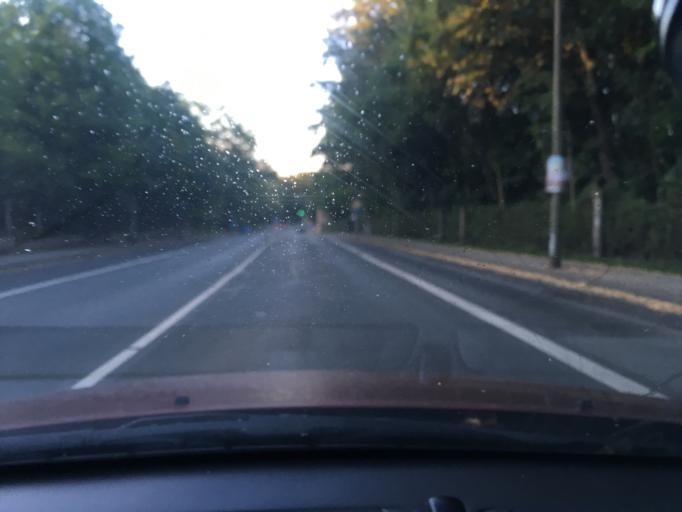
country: DE
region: Saxony
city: Goerlitz
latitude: 51.1497
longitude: 14.9945
